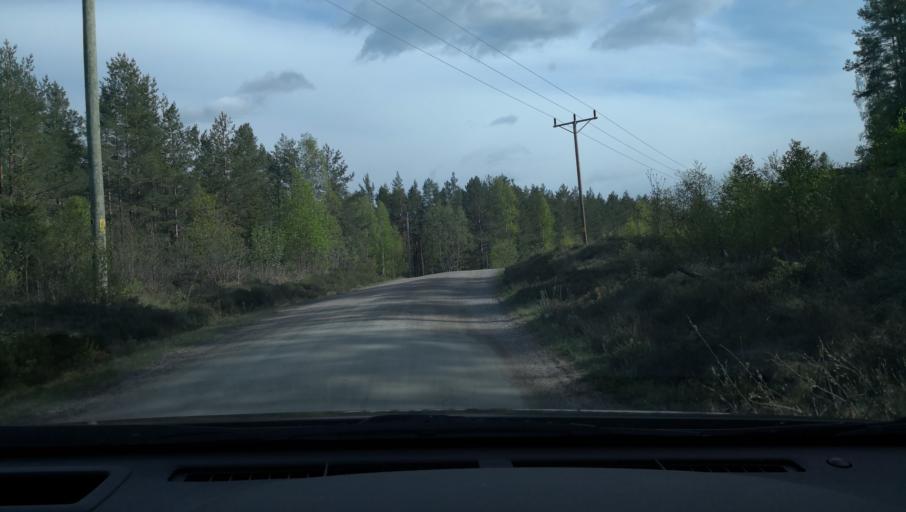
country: SE
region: OErebro
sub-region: Askersunds Kommun
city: Asbro
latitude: 59.0322
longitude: 15.0446
